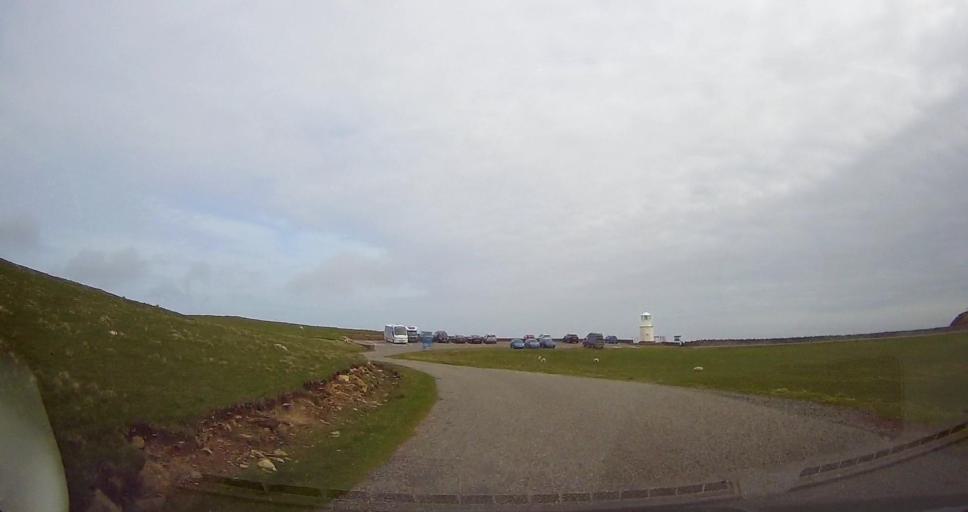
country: GB
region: Scotland
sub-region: Shetland Islands
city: Sandwick
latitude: 59.8584
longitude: -1.2740
